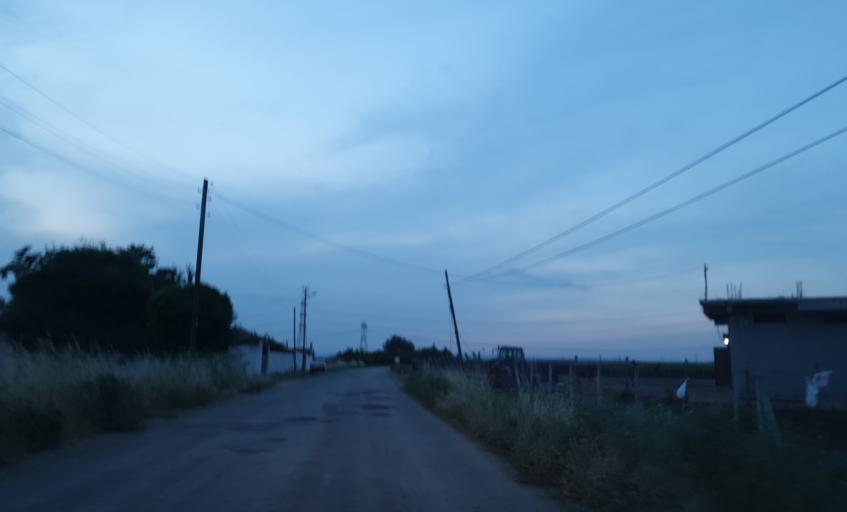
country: TR
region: Kirklareli
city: Vize
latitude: 41.4901
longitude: 27.7522
